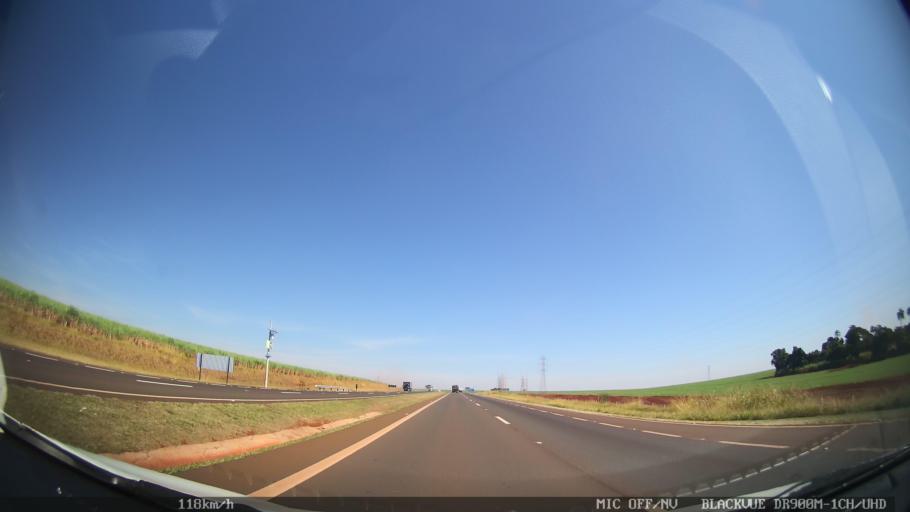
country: BR
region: Sao Paulo
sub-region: Ribeirao Preto
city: Ribeirao Preto
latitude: -21.1503
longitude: -47.8847
